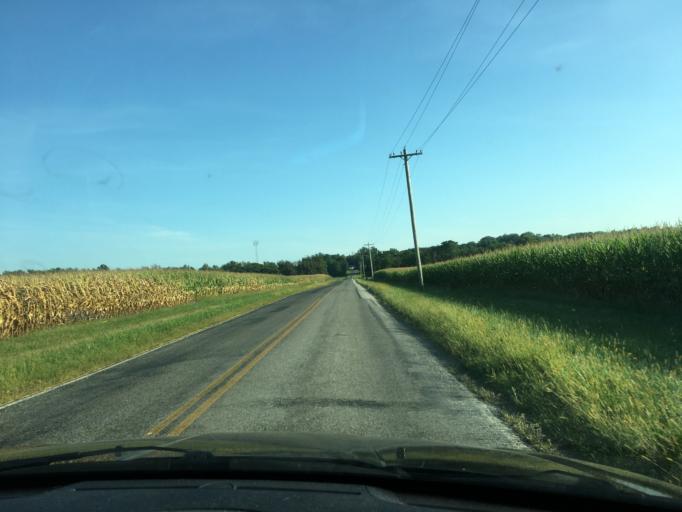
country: US
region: Ohio
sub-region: Logan County
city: West Liberty
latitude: 40.2093
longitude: -83.6688
